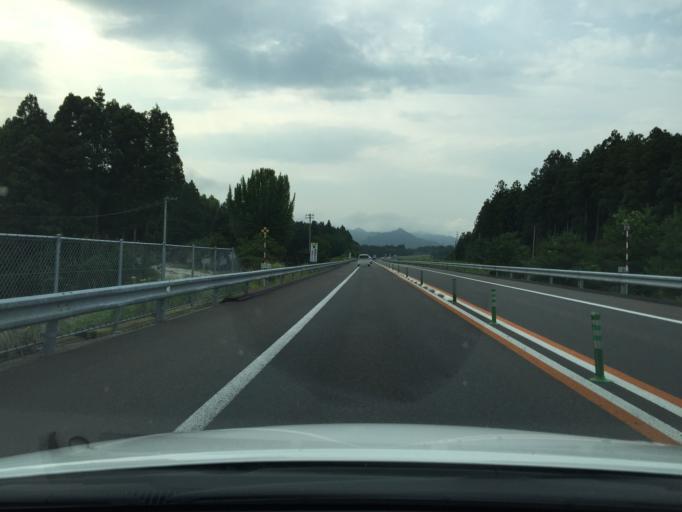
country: JP
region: Fukushima
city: Namie
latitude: 37.3508
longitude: 140.9820
